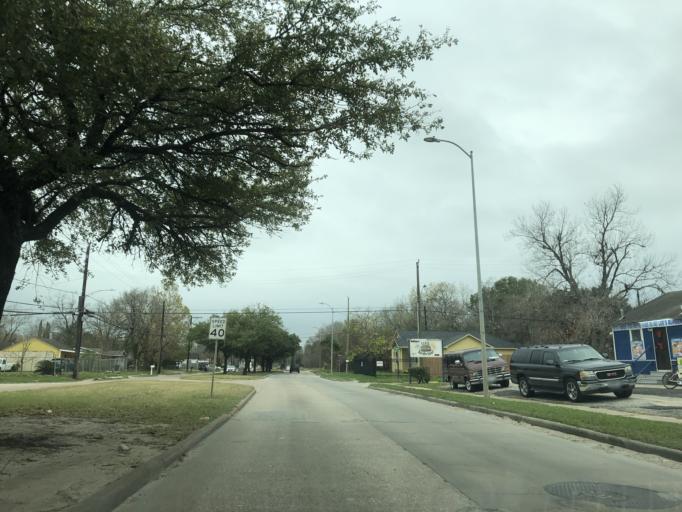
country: US
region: Texas
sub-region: Harris County
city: Jacinto City
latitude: 29.8213
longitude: -95.2845
